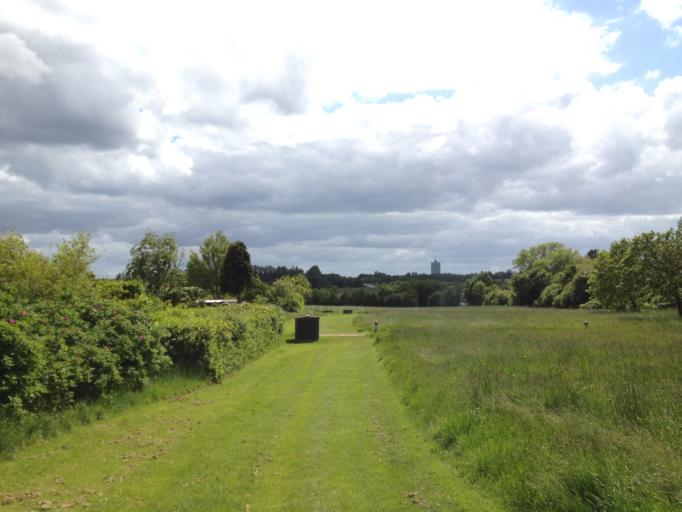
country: DK
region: Capital Region
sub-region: Fredensborg Kommune
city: Niva
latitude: 55.9332
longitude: 12.4862
